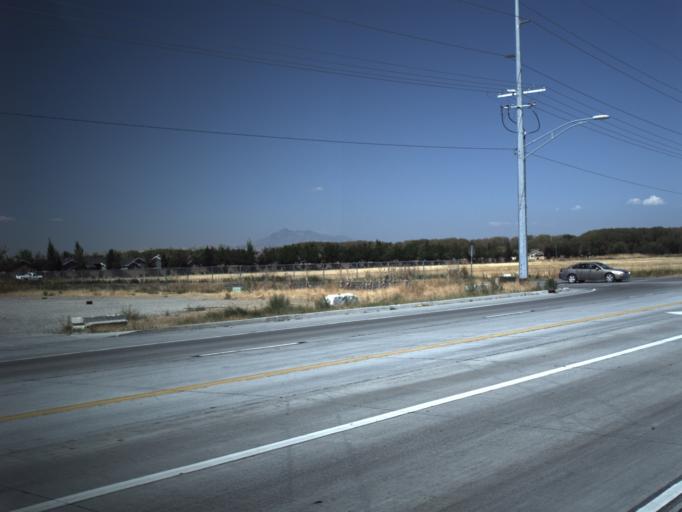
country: US
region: Utah
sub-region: Cache County
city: Nibley
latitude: 41.6995
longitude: -111.8603
